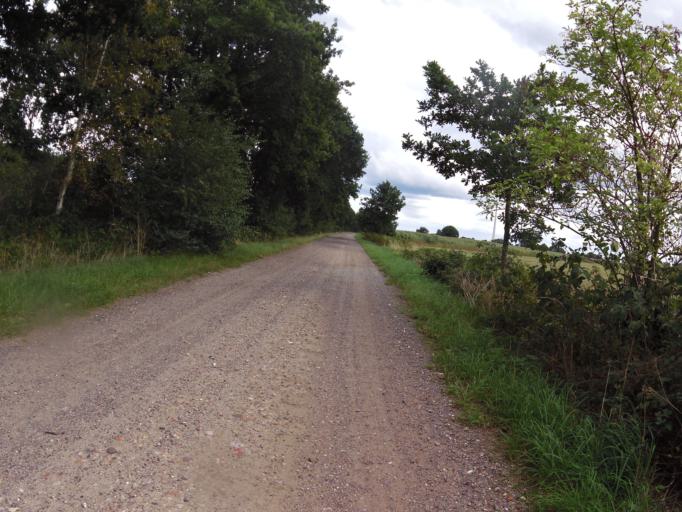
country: DE
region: Lower Saxony
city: Oerel
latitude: 53.4936
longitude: 9.0484
